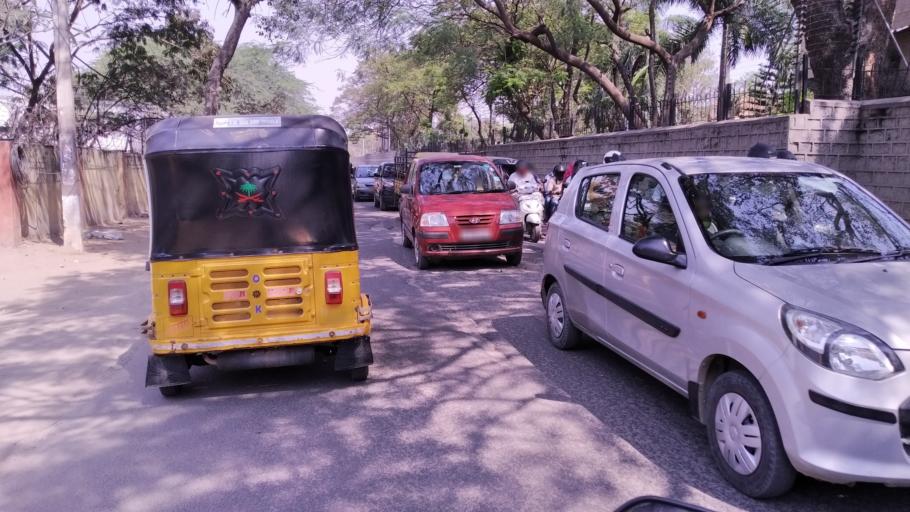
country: IN
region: Telangana
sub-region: Hyderabad
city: Malkajgiri
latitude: 17.4609
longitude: 78.4849
